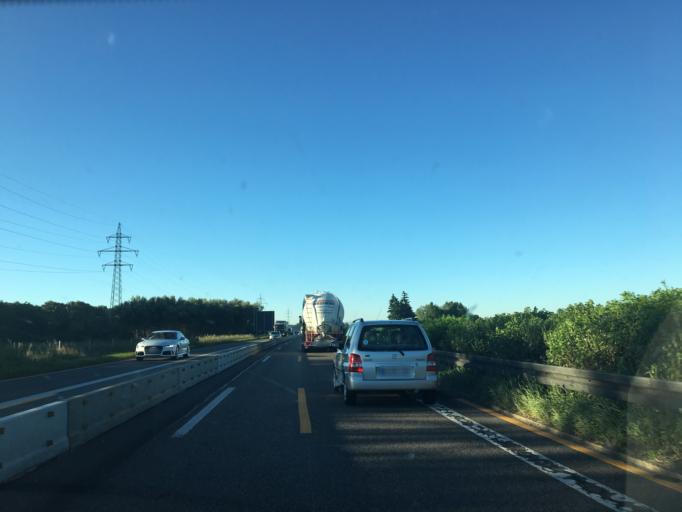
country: DE
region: Baden-Wuerttemberg
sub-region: Tuebingen Region
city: Dettingen an der Iller
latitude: 48.1014
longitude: 10.1315
